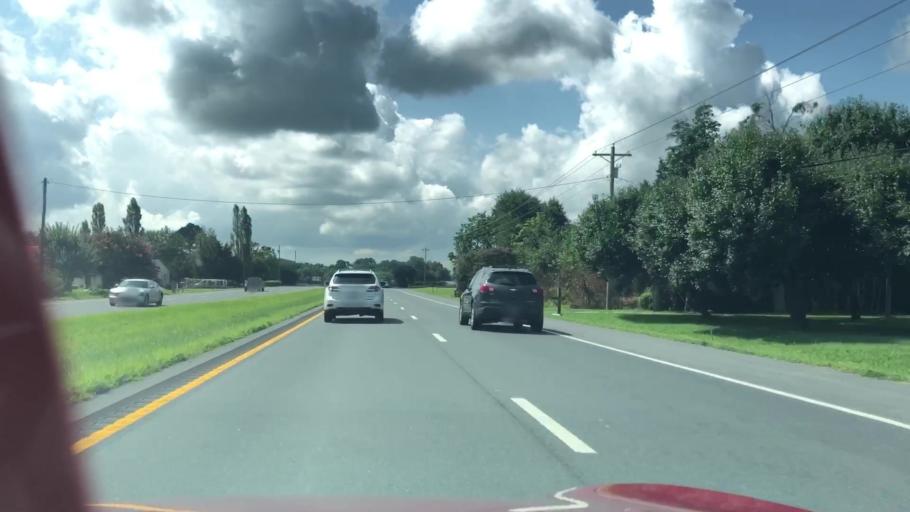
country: US
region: Virginia
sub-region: Accomack County
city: Accomac
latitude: 37.7766
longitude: -75.6113
